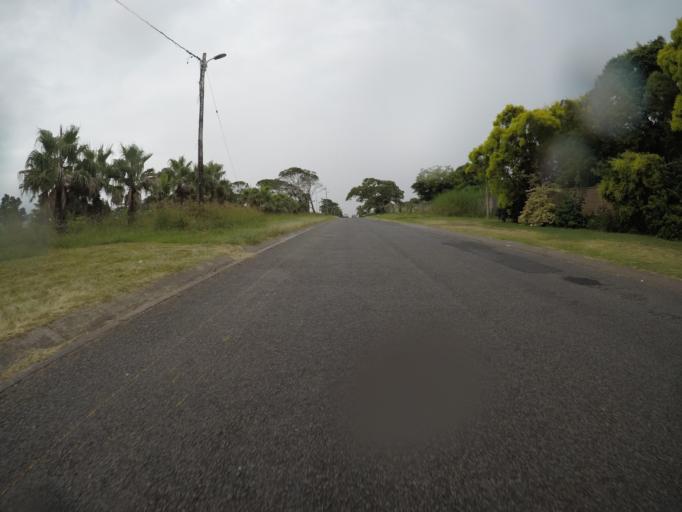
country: ZA
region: Eastern Cape
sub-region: Buffalo City Metropolitan Municipality
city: East London
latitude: -32.9852
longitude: 27.8588
